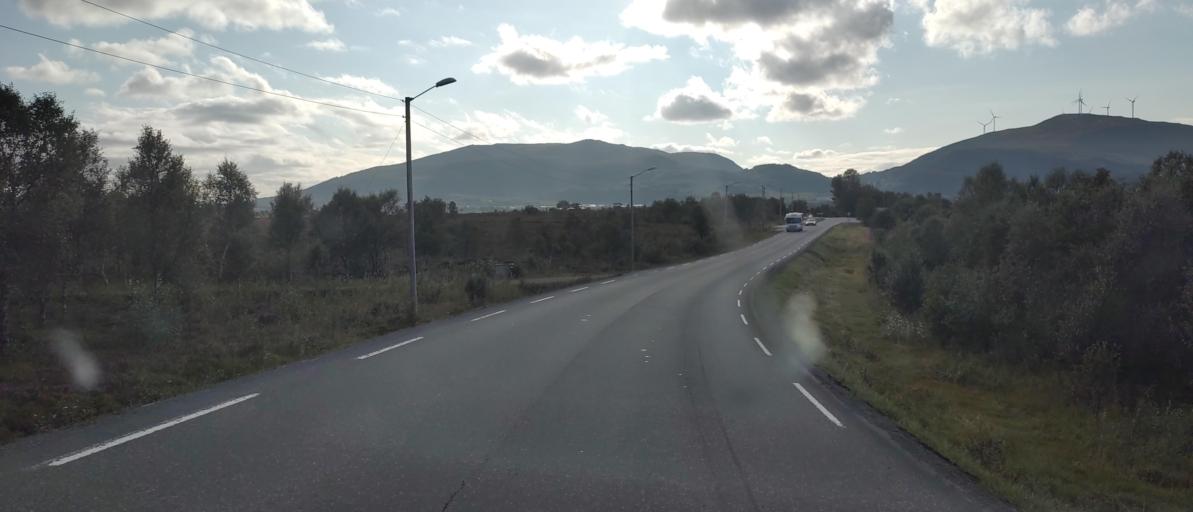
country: NO
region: Nordland
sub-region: Sortland
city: Sortland
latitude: 68.7179
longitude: 15.4529
